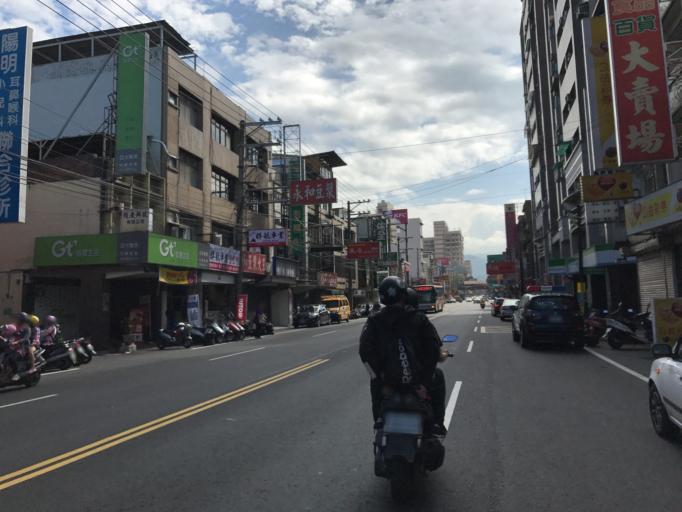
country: TW
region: Taiwan
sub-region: Hsinchu
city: Zhubei
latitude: 24.7436
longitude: 121.0835
